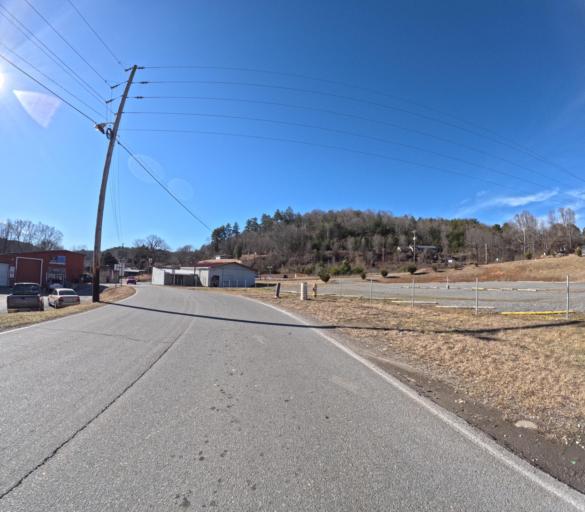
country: US
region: North Carolina
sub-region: Cherokee County
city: Murphy
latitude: 35.0947
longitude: -84.0352
